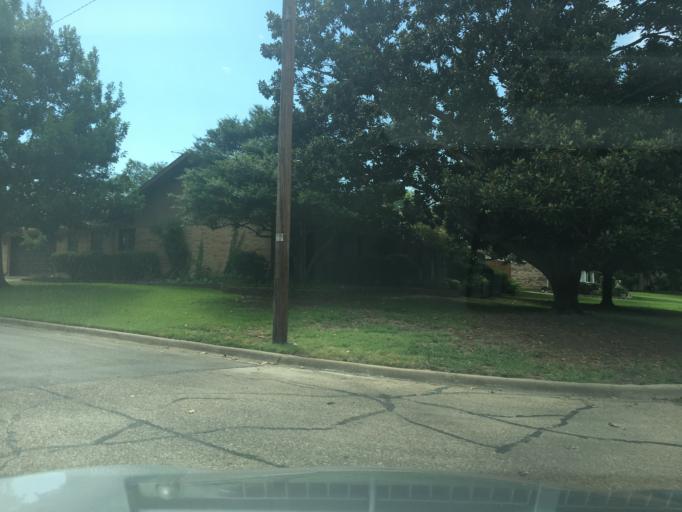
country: US
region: Texas
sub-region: Dallas County
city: Carrollton
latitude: 32.9453
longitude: -96.8588
